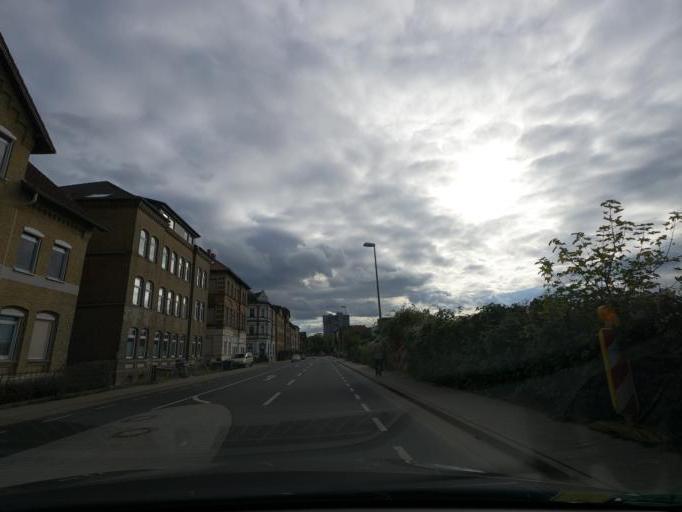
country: DE
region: Lower Saxony
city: Braunschweig
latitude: 52.2774
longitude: 10.5259
